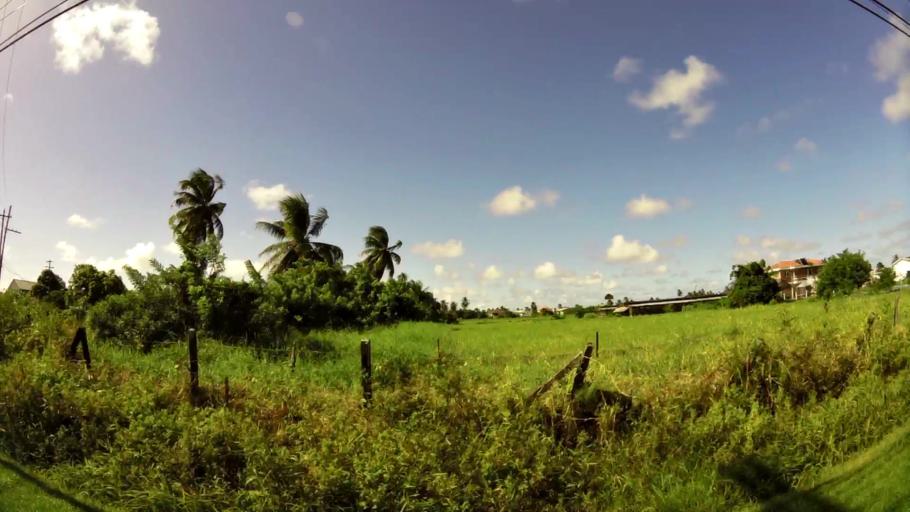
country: GY
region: Demerara-Mahaica
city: Georgetown
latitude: 6.8212
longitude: -58.1263
